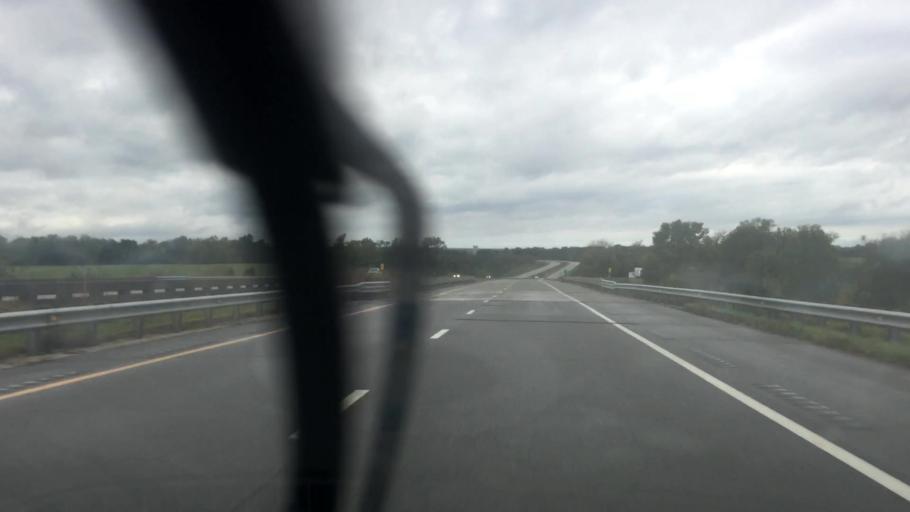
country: US
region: Kansas
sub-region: Miami County
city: Osawatomie
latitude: 38.5202
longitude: -94.9111
